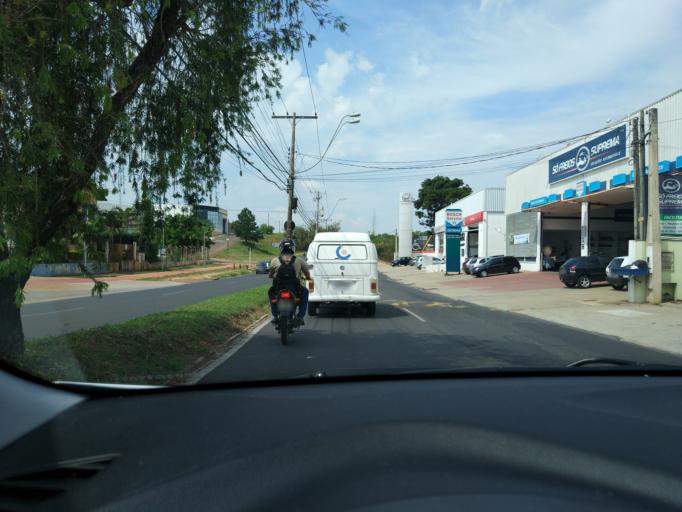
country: BR
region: Sao Paulo
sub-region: Botucatu
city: Botucatu
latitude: -22.8704
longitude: -48.4703
